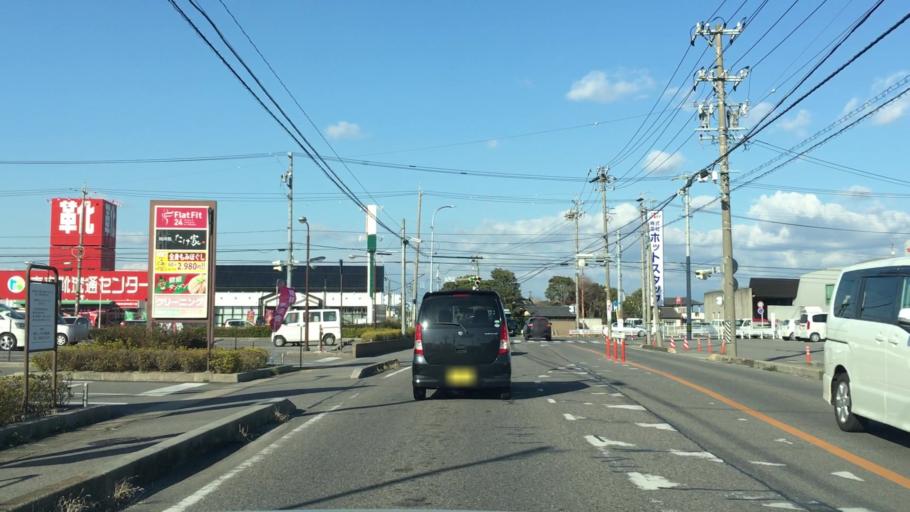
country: JP
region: Aichi
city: Nishio
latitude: 34.8598
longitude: 137.0684
